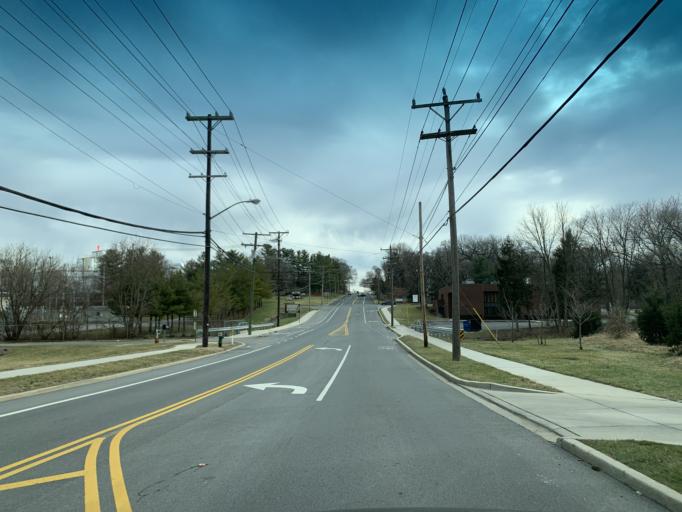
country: US
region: Maryland
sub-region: Washington County
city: Hagerstown
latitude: 39.6194
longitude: -77.7128
